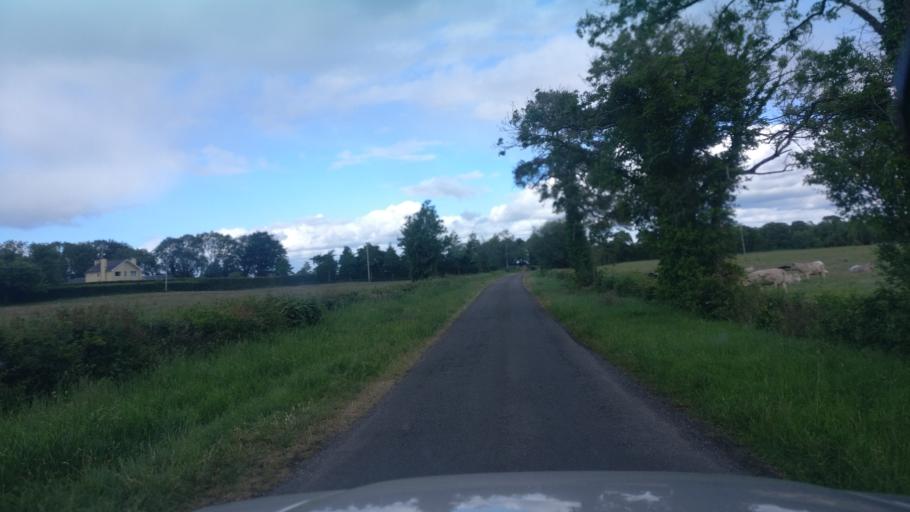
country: IE
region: Connaught
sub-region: County Galway
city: Portumna
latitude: 53.1994
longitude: -8.3471
